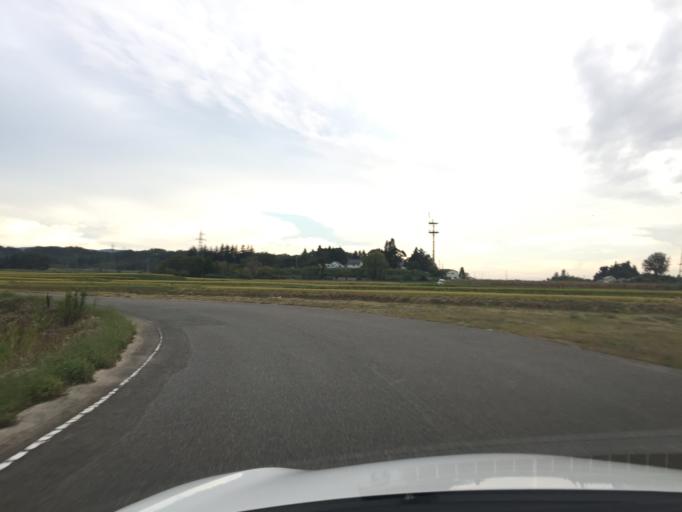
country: JP
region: Fukushima
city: Kitakata
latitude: 37.5433
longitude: 139.9664
